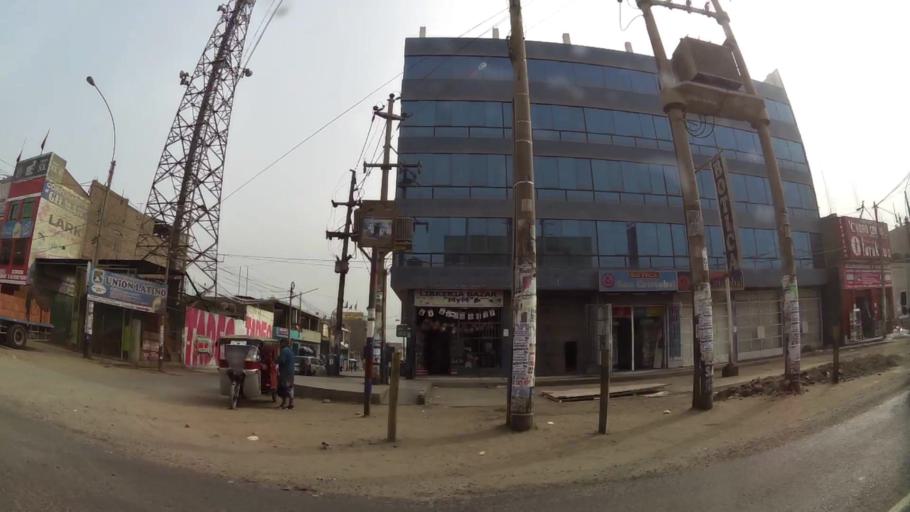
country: PE
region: Lima
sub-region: Lima
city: Santa Maria
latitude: -12.0025
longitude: -76.8373
